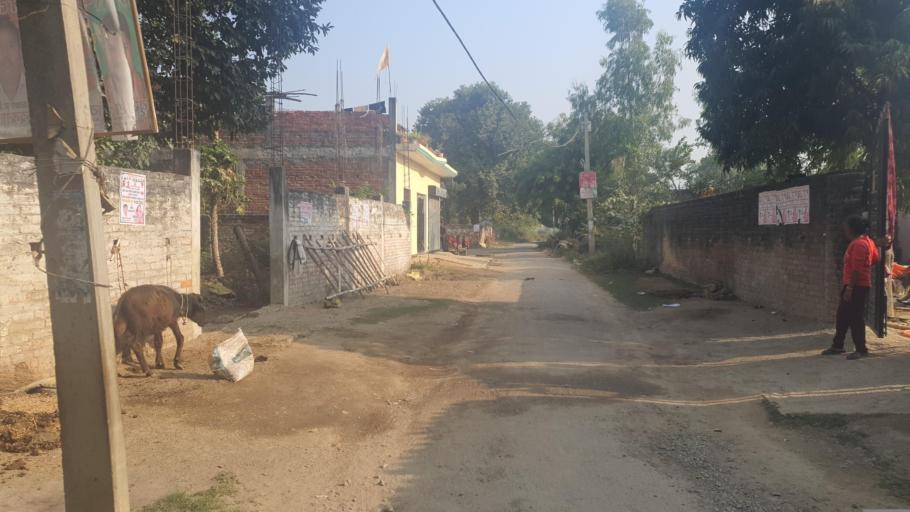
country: IN
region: Uttar Pradesh
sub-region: Lucknow District
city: Goshainganj
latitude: 26.7735
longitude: 81.0121
